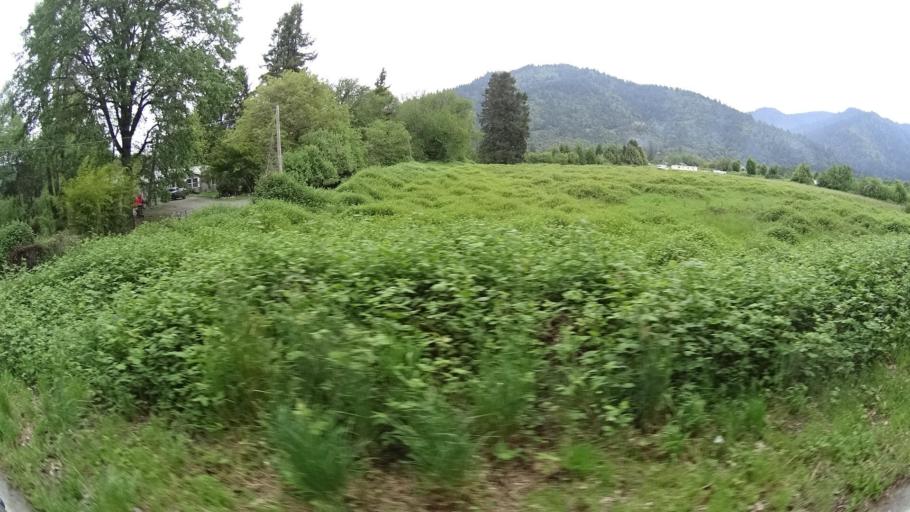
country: US
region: California
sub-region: Humboldt County
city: Willow Creek
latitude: 41.0808
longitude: -123.7013
